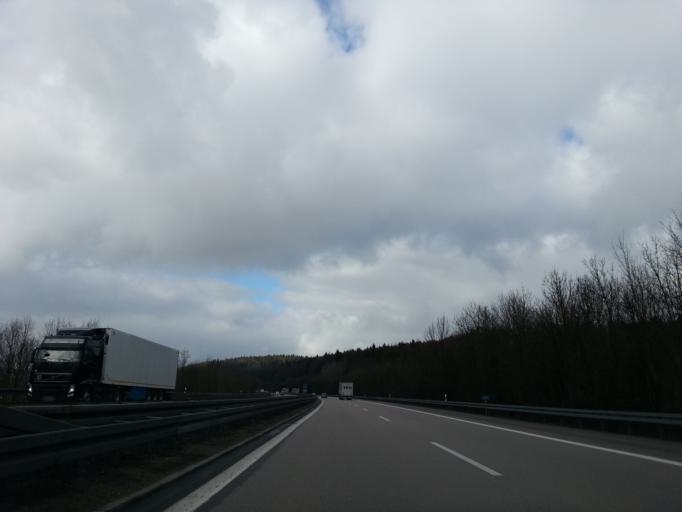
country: DE
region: Bavaria
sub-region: Upper Palatinate
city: Velburg
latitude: 49.2167
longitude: 11.6490
